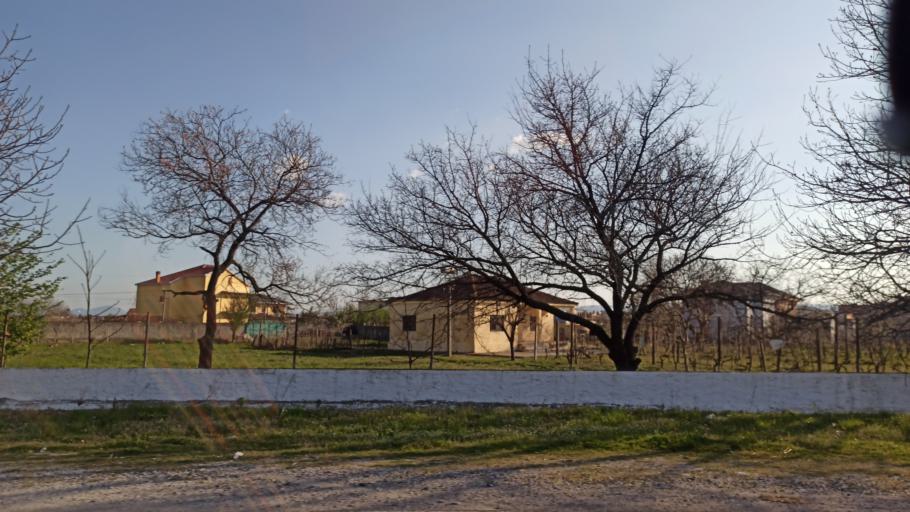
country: AL
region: Shkoder
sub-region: Rrethi i Shkodres
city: Vau i Dejes
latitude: 41.9897
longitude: 19.5869
